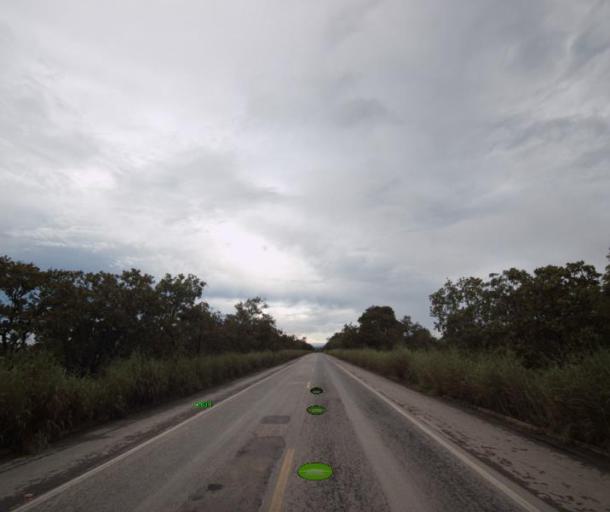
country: BR
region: Goias
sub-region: Porangatu
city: Porangatu
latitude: -13.5404
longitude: -49.1058
